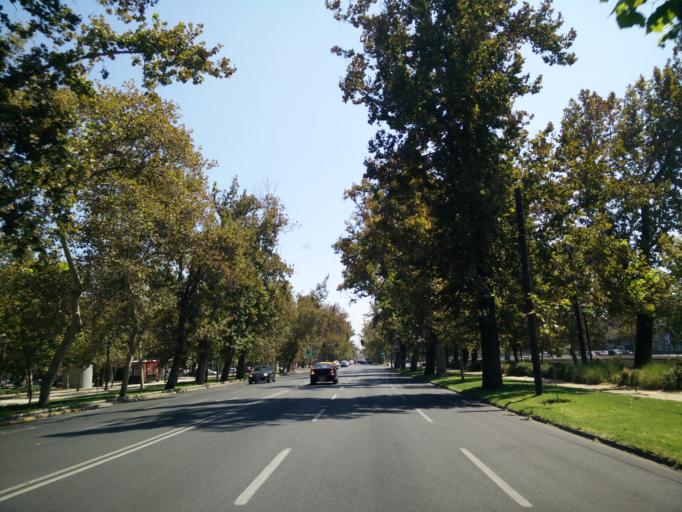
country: CL
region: Santiago Metropolitan
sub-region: Provincia de Santiago
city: Santiago
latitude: -33.4349
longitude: -70.6414
